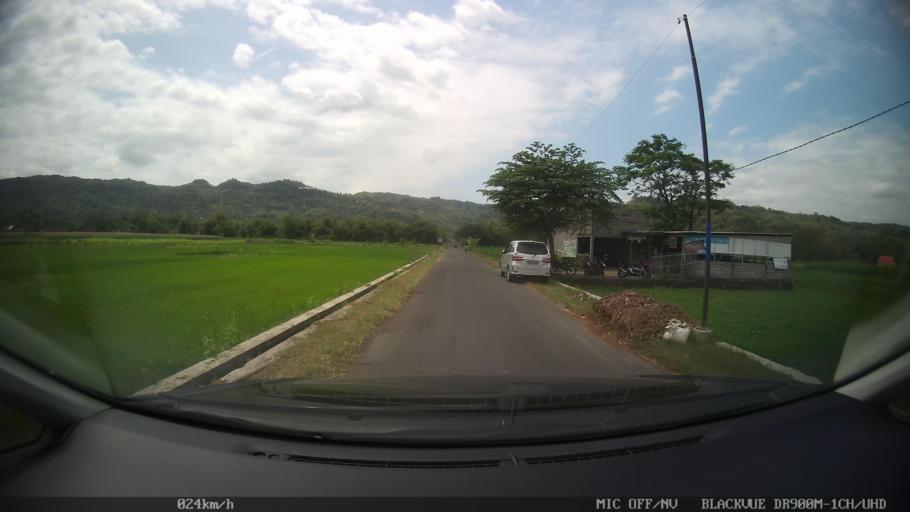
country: ID
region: Central Java
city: Candi Prambanan
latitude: -7.8102
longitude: 110.5005
